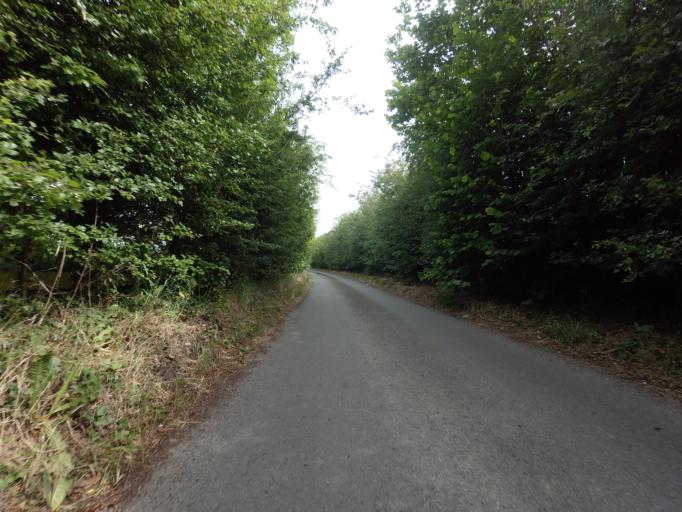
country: GB
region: England
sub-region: Kent
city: Swanley
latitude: 51.4050
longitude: 0.2084
